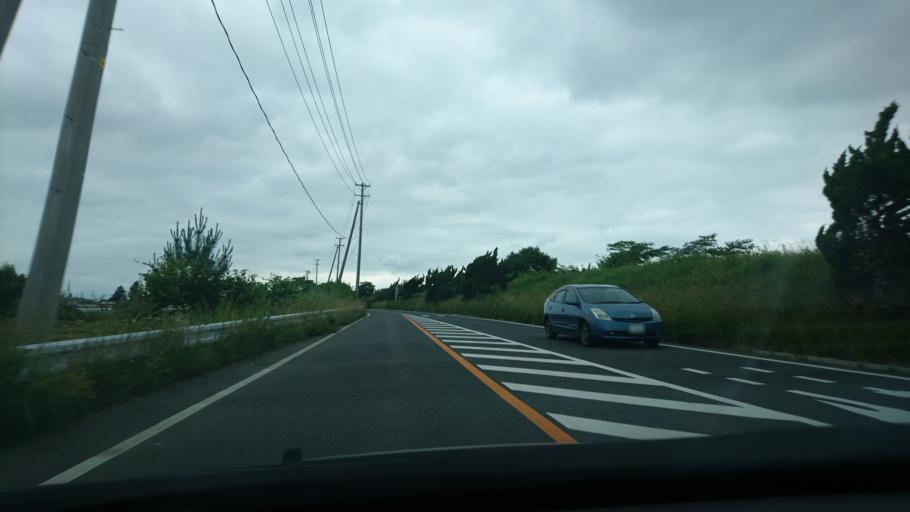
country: JP
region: Iwate
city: Ichinoseki
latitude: 38.7460
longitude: 141.1494
